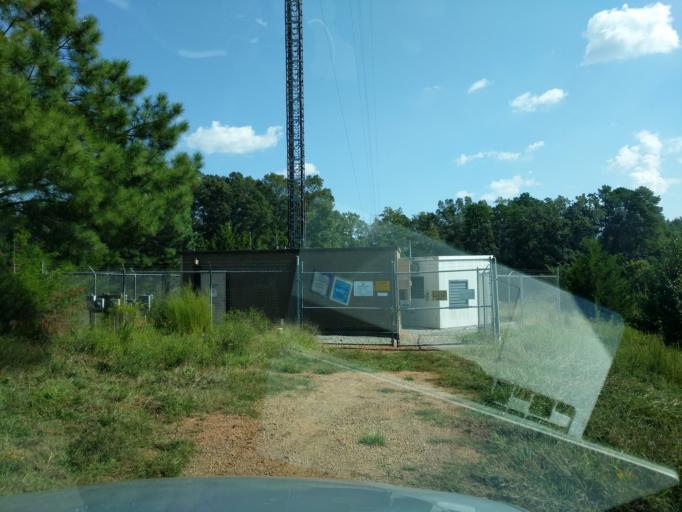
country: US
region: South Carolina
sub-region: Oconee County
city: Utica
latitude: 34.7096
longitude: -82.9248
